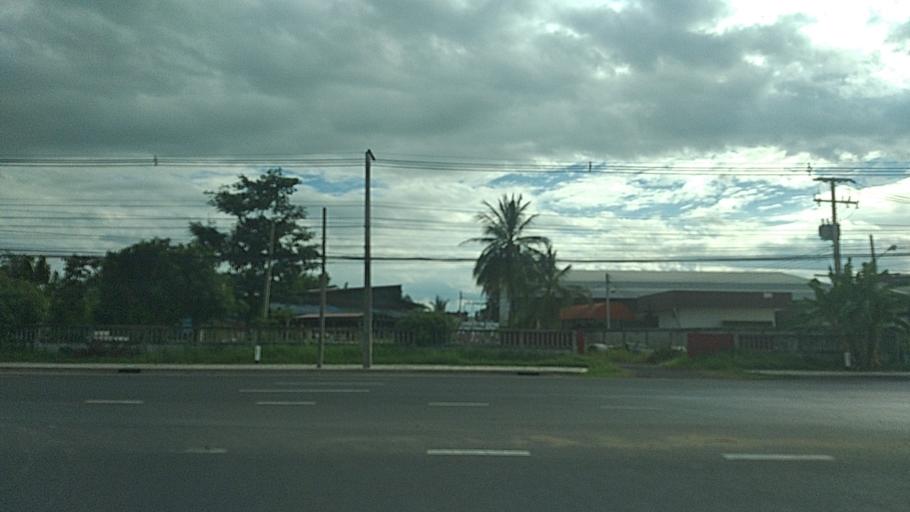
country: TH
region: Surin
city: Prasat
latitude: 14.6211
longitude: 103.4126
